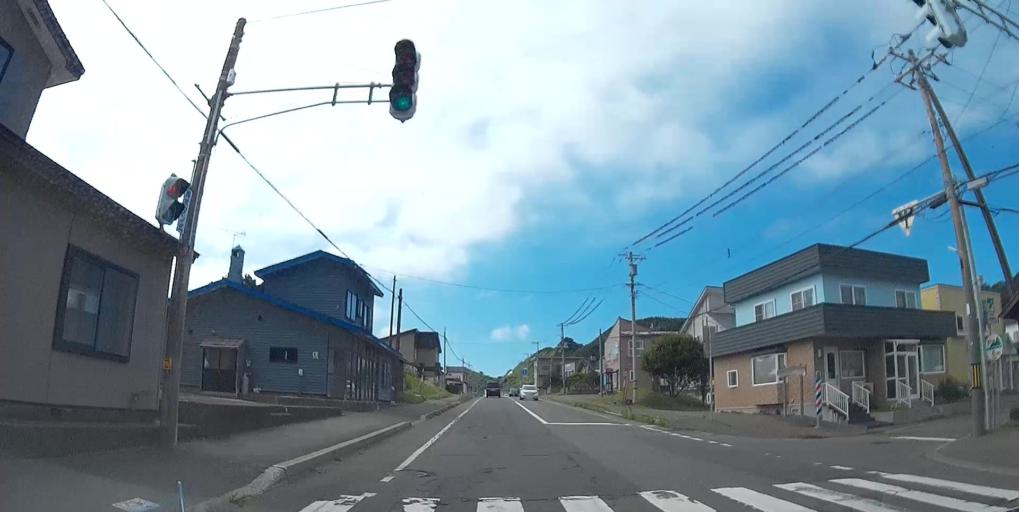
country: JP
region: Hokkaido
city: Kamiiso
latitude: 41.9748
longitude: 140.1383
